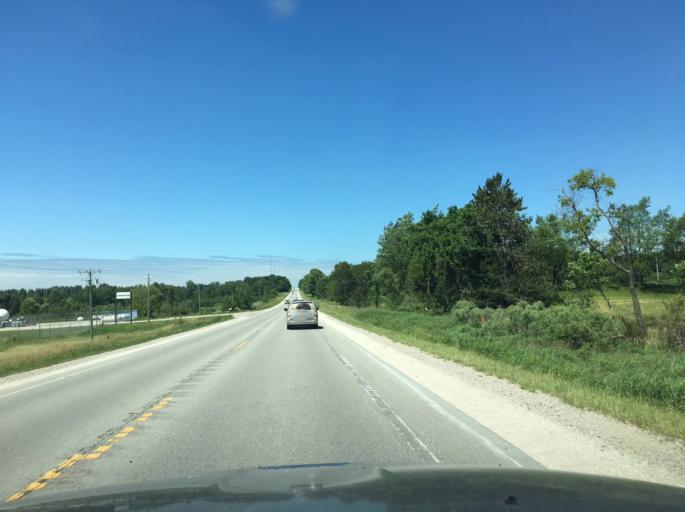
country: US
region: Michigan
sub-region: Osceola County
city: Reed City
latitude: 43.8877
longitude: -85.5711
